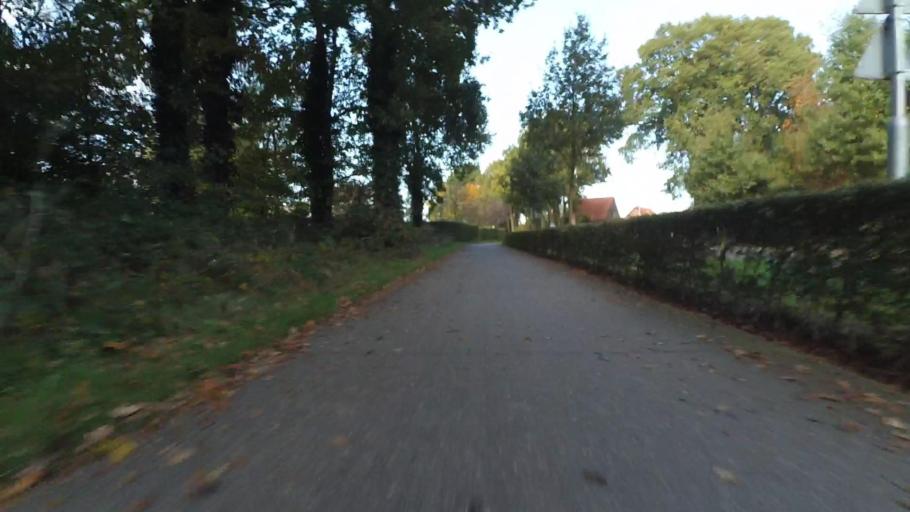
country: NL
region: Gelderland
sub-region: Gemeente Ermelo
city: Horst
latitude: 52.3107
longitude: 5.5925
